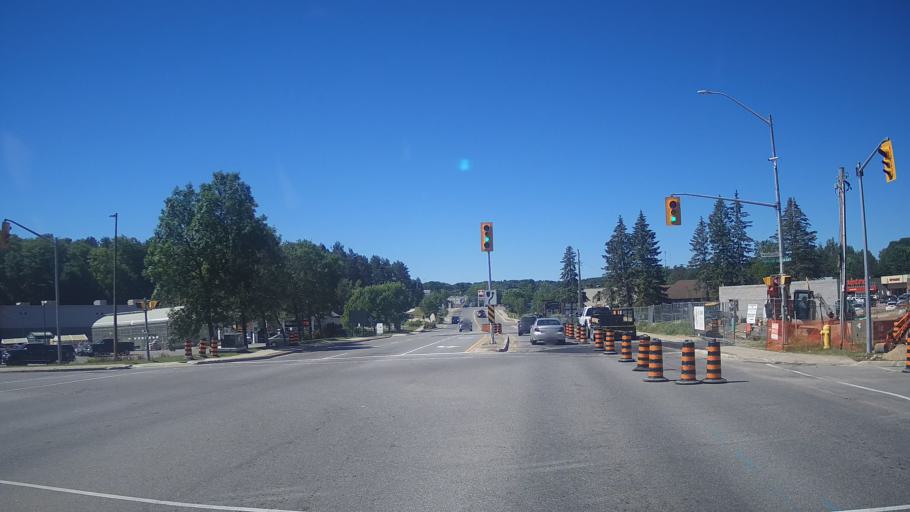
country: CA
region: Ontario
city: Huntsville
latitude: 45.3354
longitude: -79.2049
